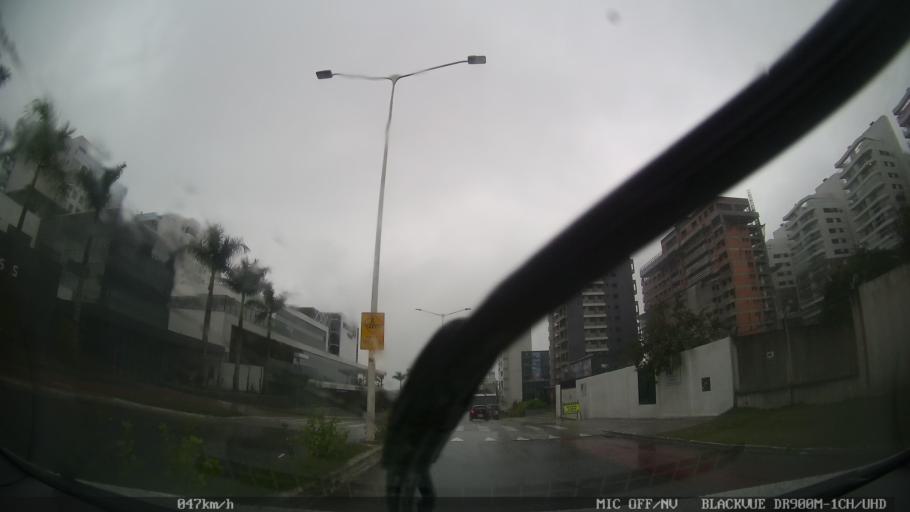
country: BR
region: Santa Catarina
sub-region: Balneario Camboriu
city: Balneario Camboriu
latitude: -26.9450
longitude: -48.6315
